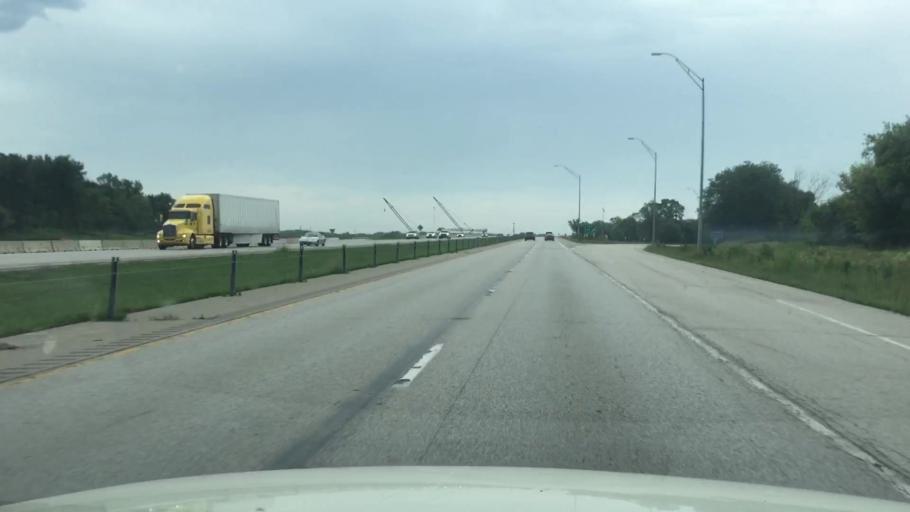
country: US
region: Iowa
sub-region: Polk County
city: Ankeny
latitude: 41.7364
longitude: -93.5779
